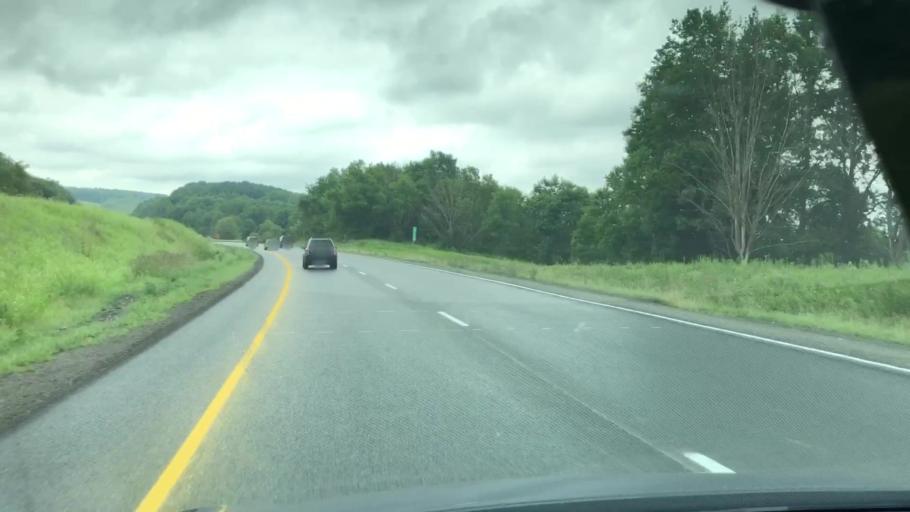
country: US
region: Pennsylvania
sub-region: Butler County
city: Prospect
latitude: 40.9285
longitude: -80.1317
